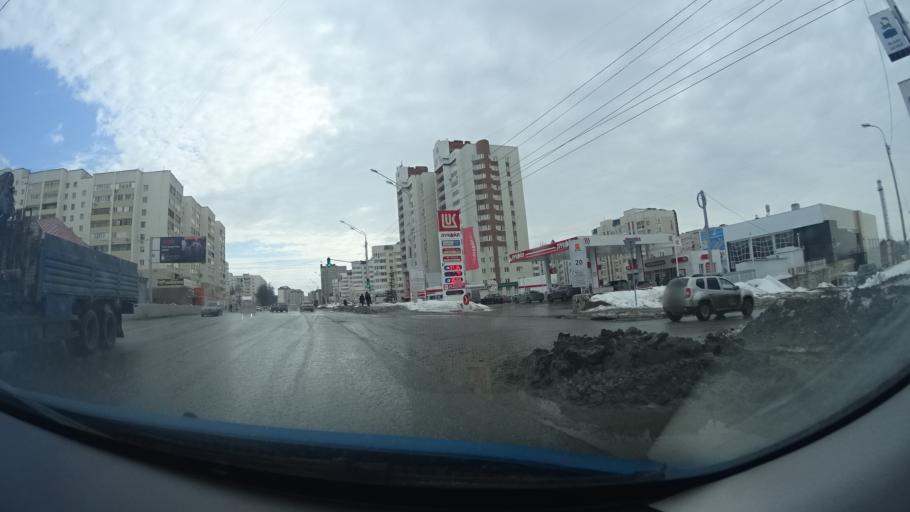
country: RU
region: Bashkortostan
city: Ufa
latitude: 54.6993
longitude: 55.9837
